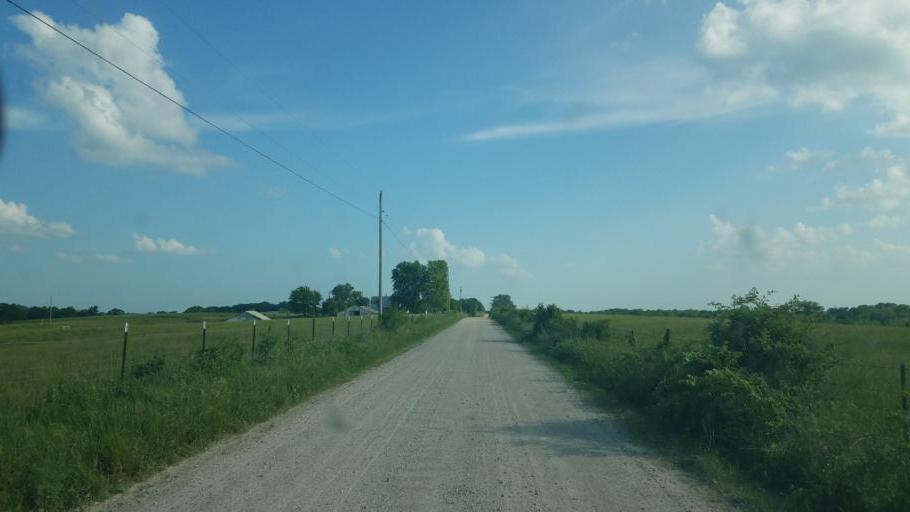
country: US
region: Missouri
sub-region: Moniteau County
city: California
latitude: 38.7547
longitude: -92.6055
